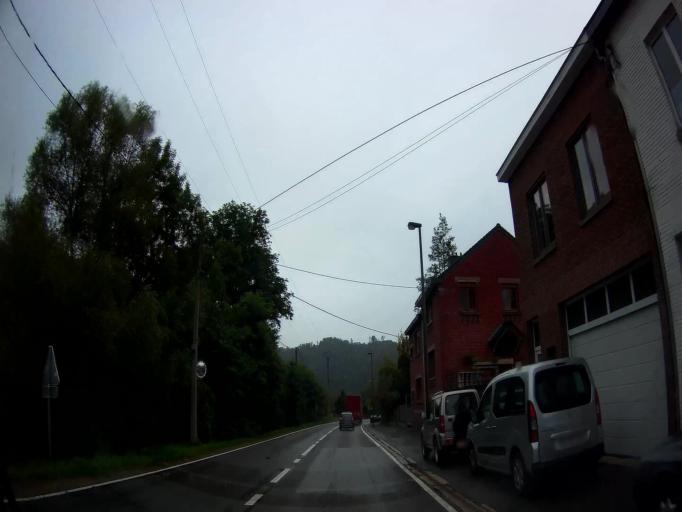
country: BE
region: Wallonia
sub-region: Province de Liege
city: Olne
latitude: 50.5672
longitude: 5.7633
